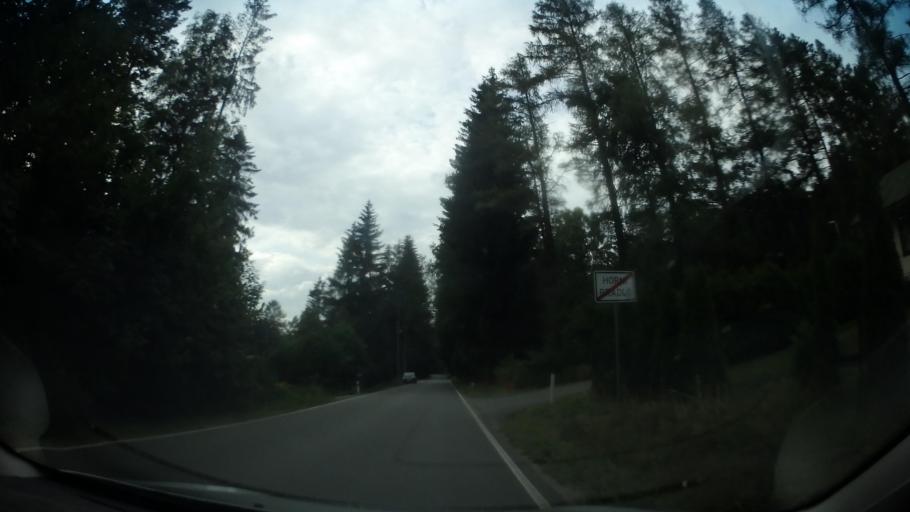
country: CZ
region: Pardubicky
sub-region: Okres Chrudim
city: Nasavrky
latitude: 49.8063
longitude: 15.7303
